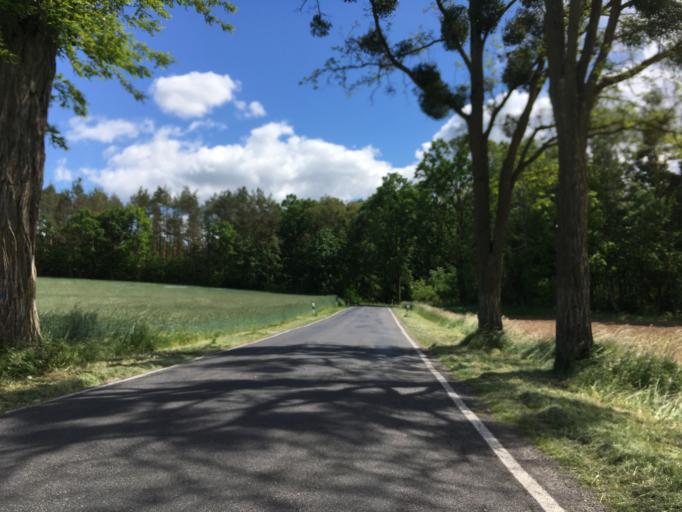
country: DE
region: Brandenburg
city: Protzel
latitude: 52.6999
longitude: 14.0205
